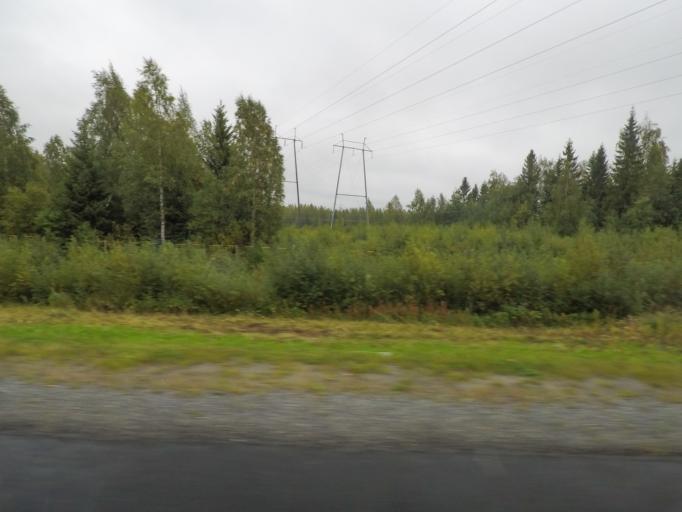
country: FI
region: Northern Savo
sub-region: Kuopio
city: Kuopio
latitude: 62.7732
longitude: 27.5868
